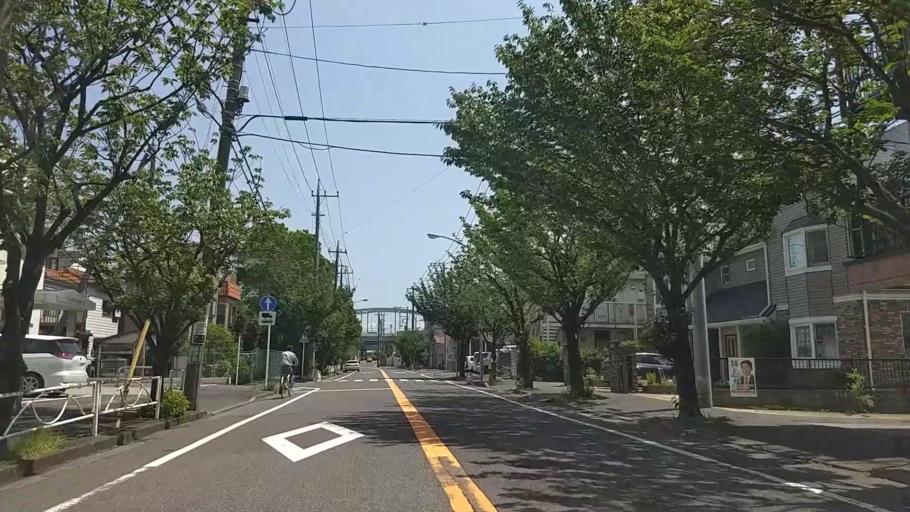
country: JP
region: Kanagawa
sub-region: Kawasaki-shi
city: Kawasaki
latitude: 35.5181
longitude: 139.7213
